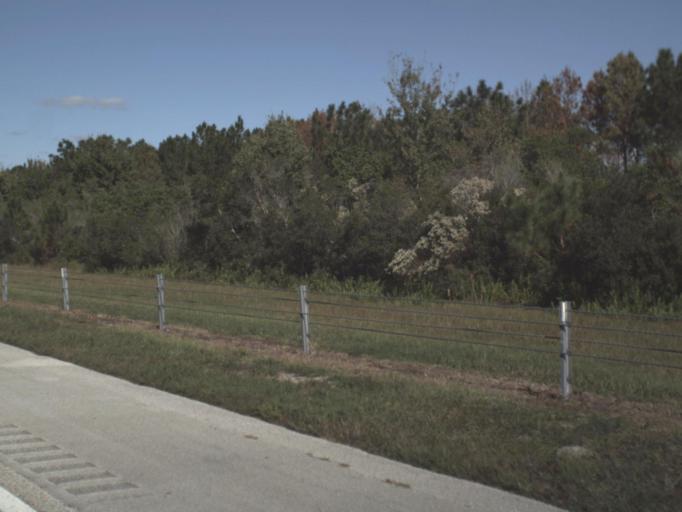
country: US
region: Florida
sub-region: Osceola County
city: Saint Cloud
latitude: 28.0151
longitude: -81.1730
